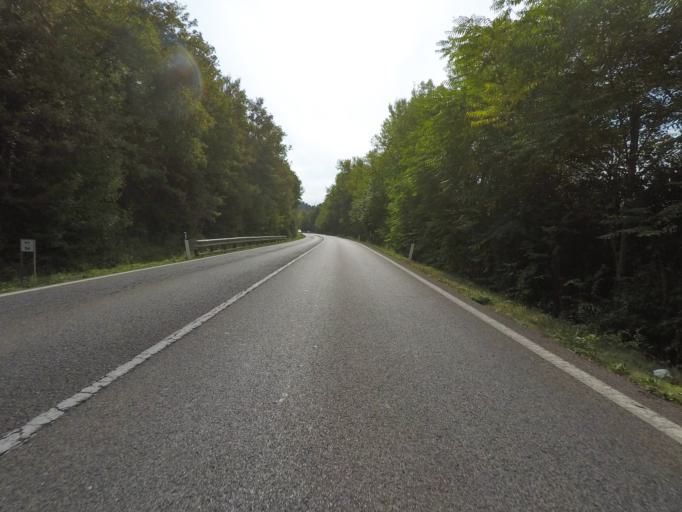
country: IT
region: Tuscany
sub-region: Provincia di Siena
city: Rosia
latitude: 43.1952
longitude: 11.2767
